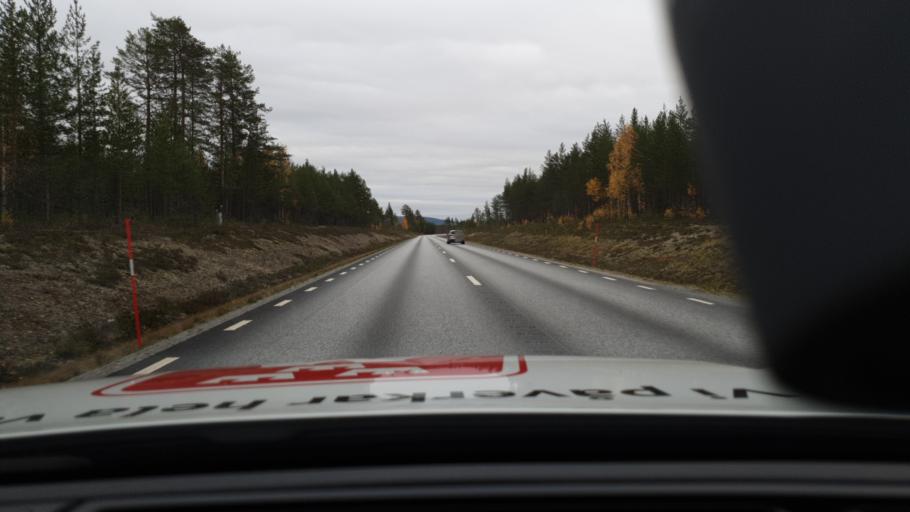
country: SE
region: Norrbotten
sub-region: Overkalix Kommun
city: OEverkalix
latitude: 66.5341
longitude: 22.3941
